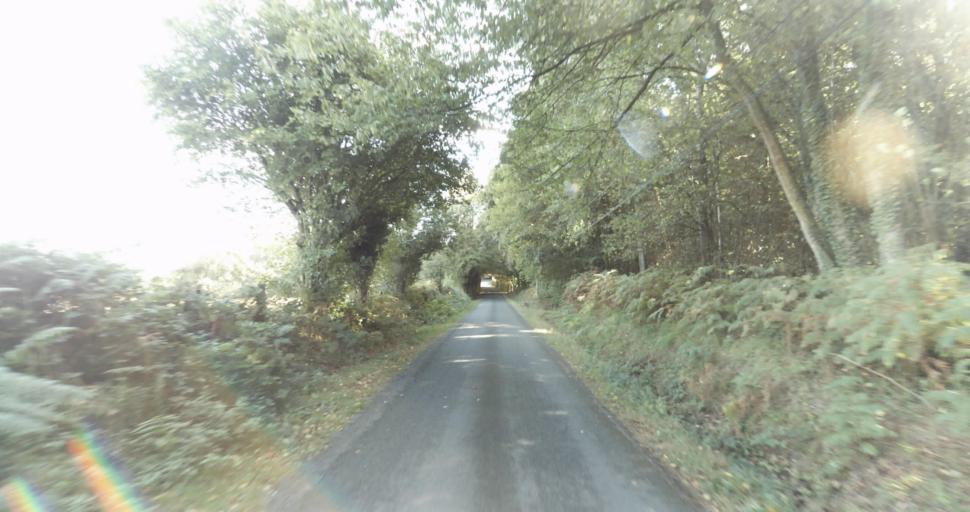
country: FR
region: Lower Normandy
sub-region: Departement de l'Orne
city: Vimoutiers
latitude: 48.9109
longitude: 0.1511
